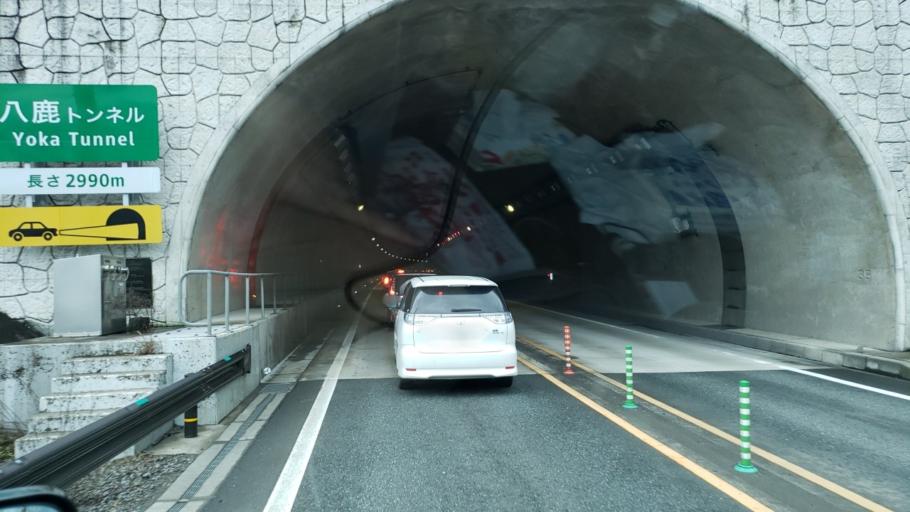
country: JP
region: Hyogo
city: Toyooka
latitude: 35.3888
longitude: 134.7503
